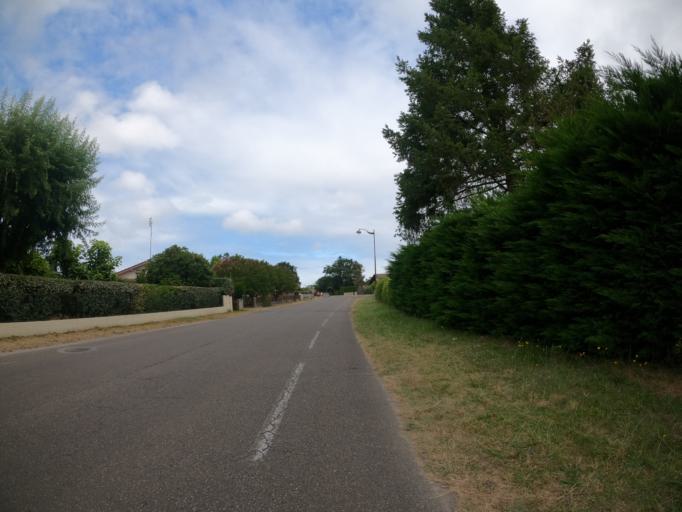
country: FR
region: Aquitaine
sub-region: Departement des Landes
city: Leon
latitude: 43.8805
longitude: -1.3050
